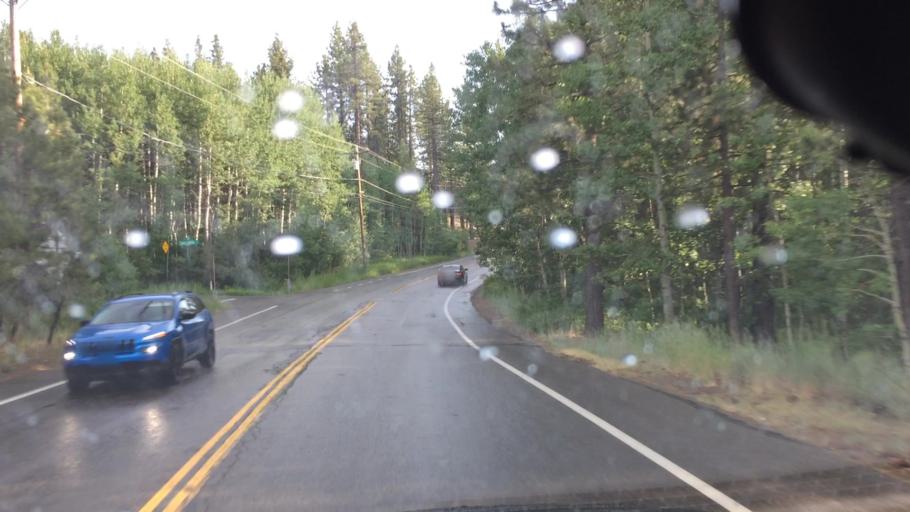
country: US
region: California
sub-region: El Dorado County
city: South Lake Tahoe
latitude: 38.9399
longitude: -119.9529
